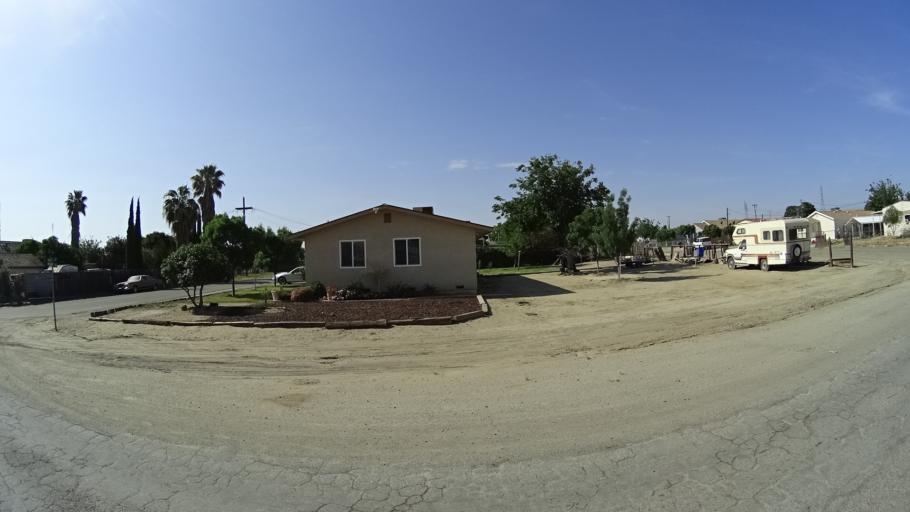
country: US
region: California
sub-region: Kings County
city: Kettleman City
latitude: 36.0103
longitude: -119.9666
